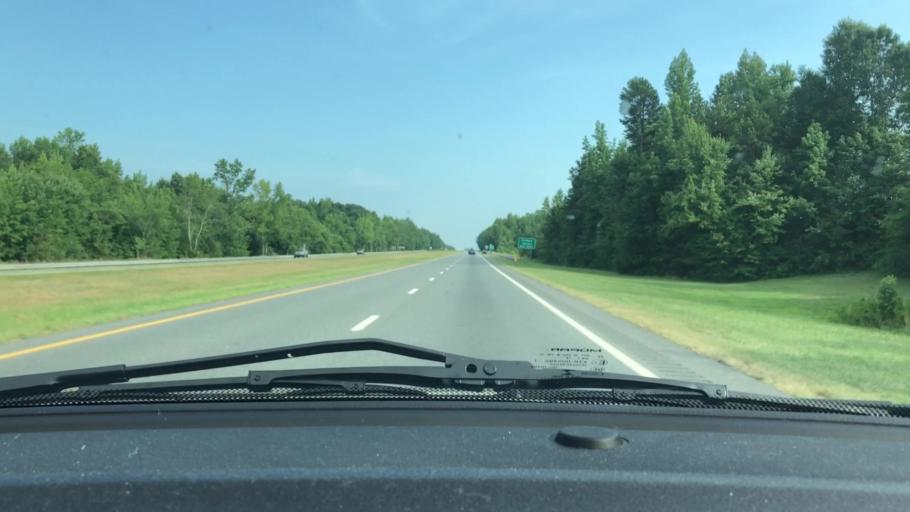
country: US
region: North Carolina
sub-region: Guilford County
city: Forest Oaks
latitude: 35.9325
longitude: -79.6831
